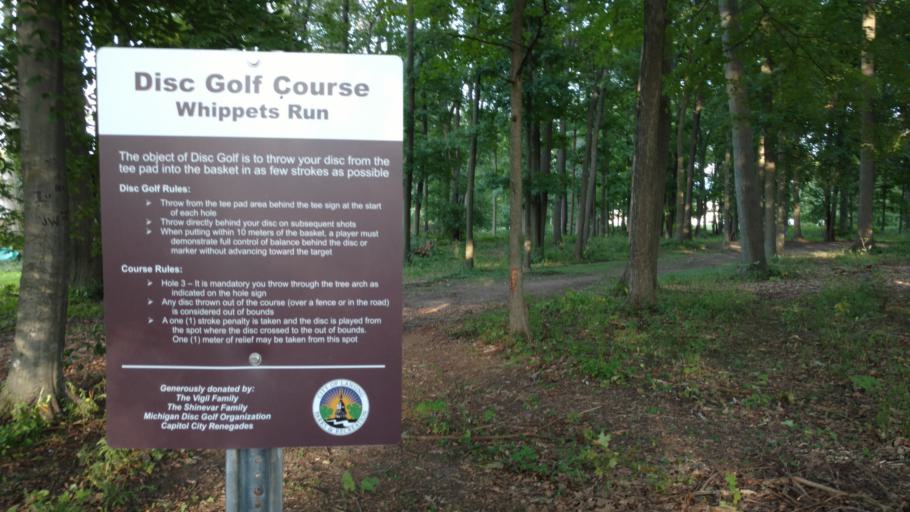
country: US
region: Michigan
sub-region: Ingham County
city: Edgemont Park
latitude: 42.7046
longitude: -84.5894
